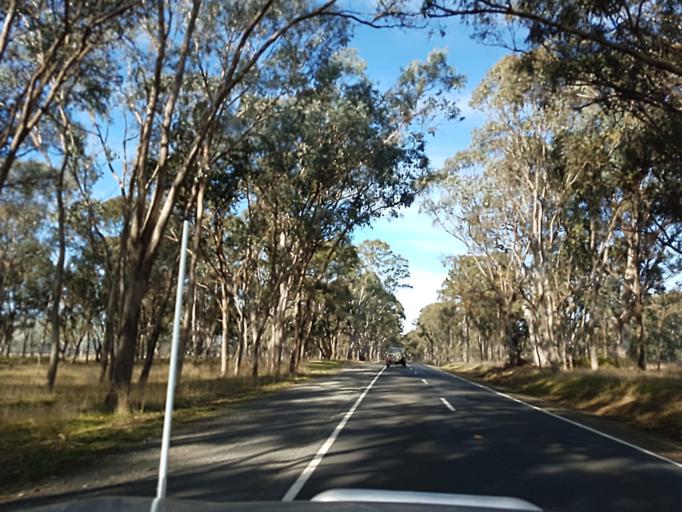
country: AU
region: Victoria
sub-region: Murrindindi
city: Alexandra
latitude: -37.1448
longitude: 145.6345
